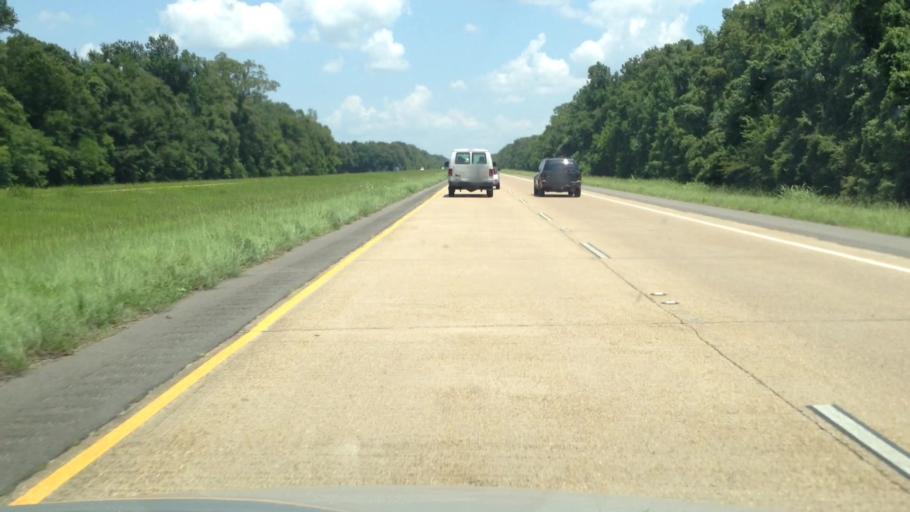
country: US
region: Louisiana
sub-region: Rapides Parish
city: Lecompte
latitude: 31.0000
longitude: -92.3393
